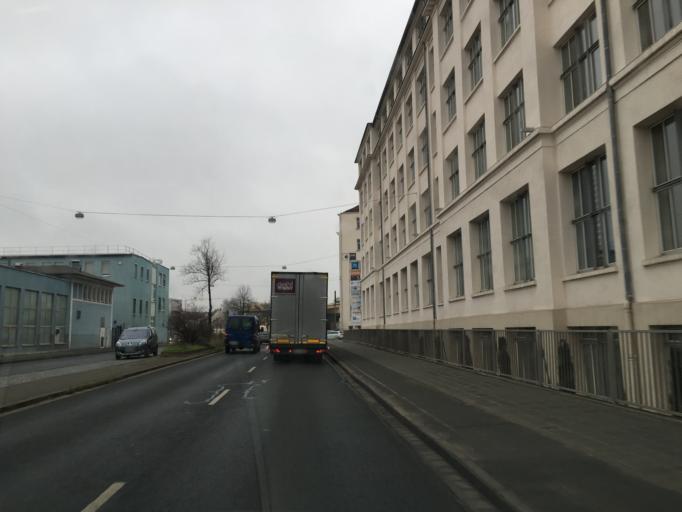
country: DE
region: Bavaria
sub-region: Regierungsbezirk Mittelfranken
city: Nuernberg
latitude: 49.4300
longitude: 11.0735
